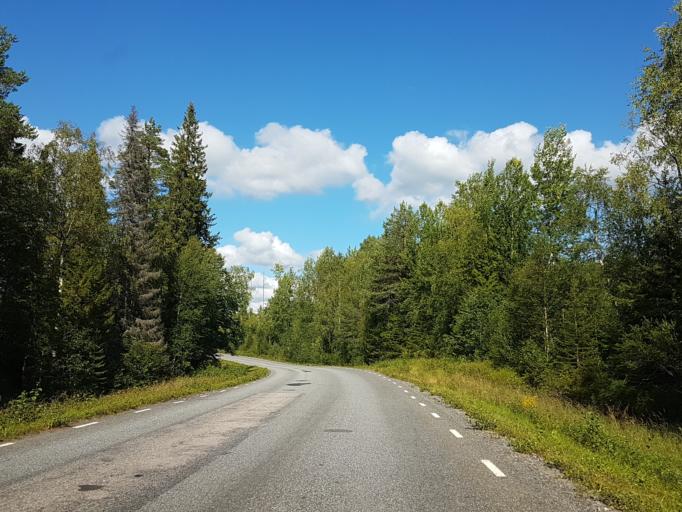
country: SE
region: Vaesterbotten
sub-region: Skelleftea Kommun
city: Burtraesk
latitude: 64.2352
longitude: 20.4774
